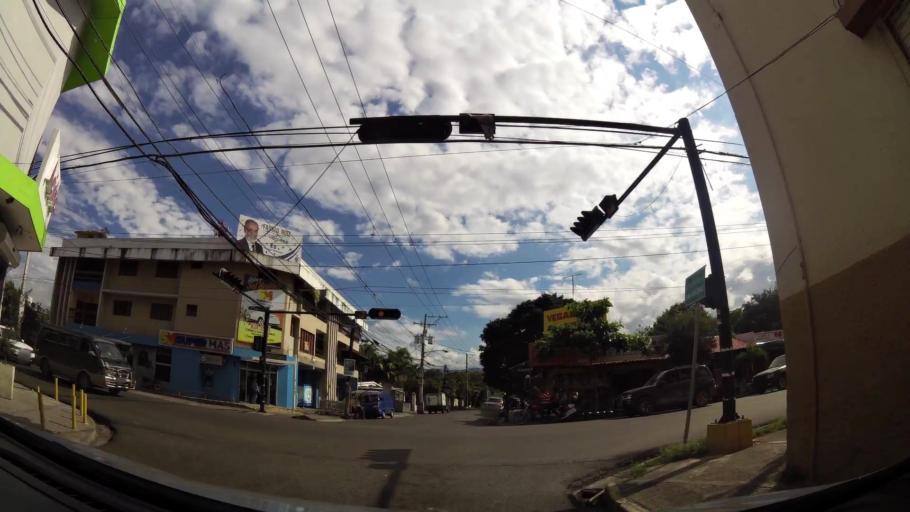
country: DO
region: La Vega
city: Concepcion de La Vega
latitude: 19.2253
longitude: -70.5255
